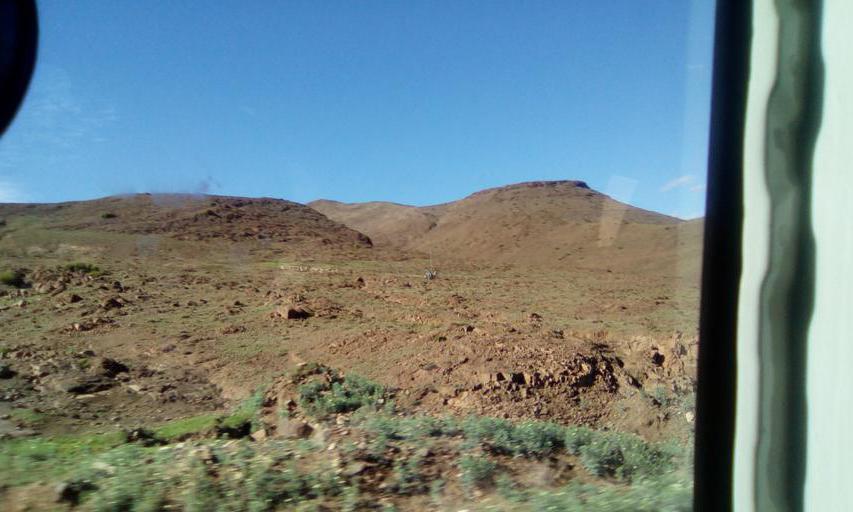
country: LS
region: Qacha's Nek
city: Qacha's Nek
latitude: -30.0453
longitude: 28.2786
